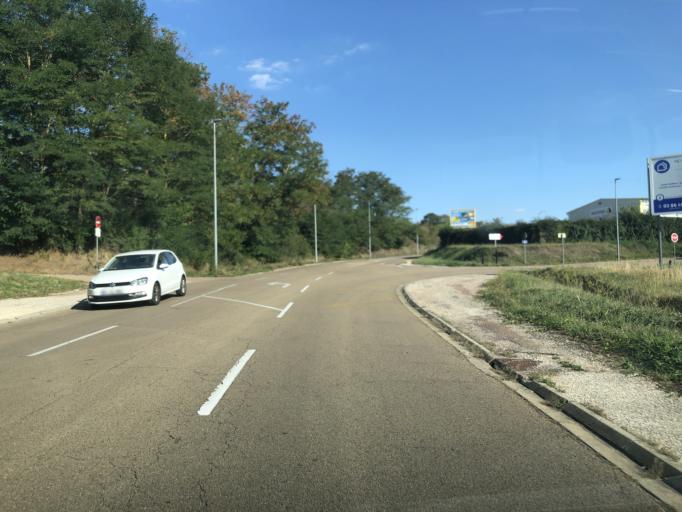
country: FR
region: Bourgogne
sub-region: Departement de l'Yonne
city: Auxerre
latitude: 47.8060
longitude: 3.5886
